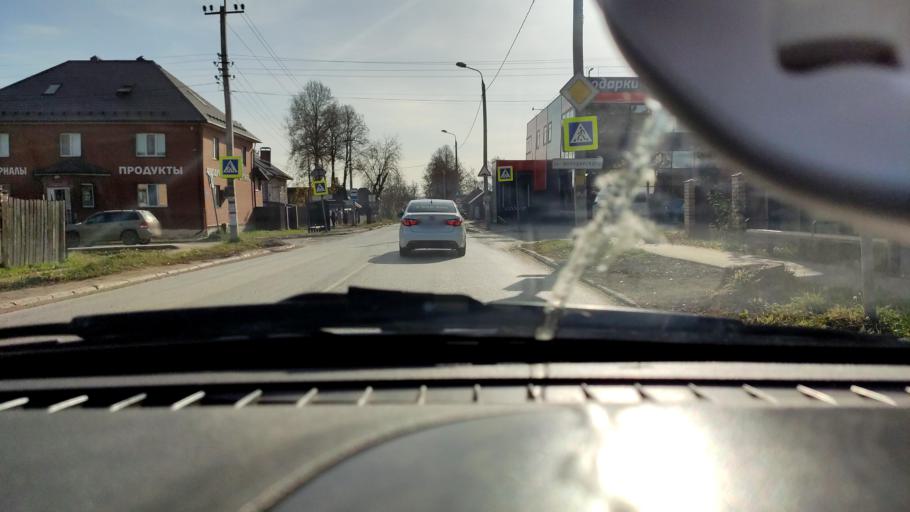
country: RU
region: Perm
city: Perm
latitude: 58.0260
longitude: 56.3328
